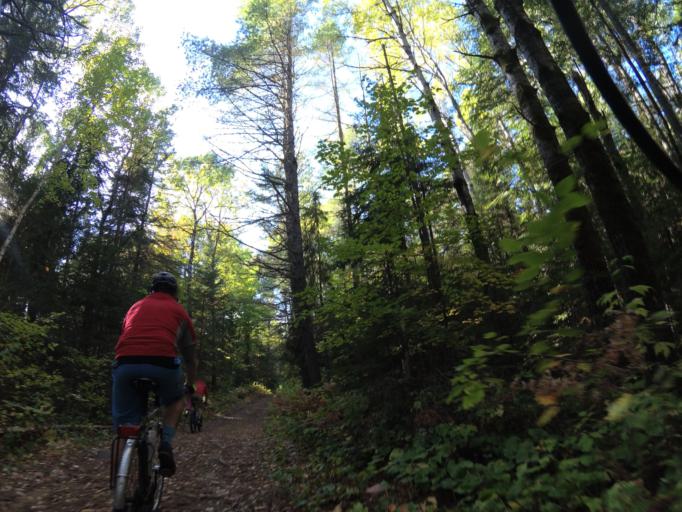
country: CA
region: Ontario
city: Pembroke
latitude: 45.3383
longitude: -77.1672
